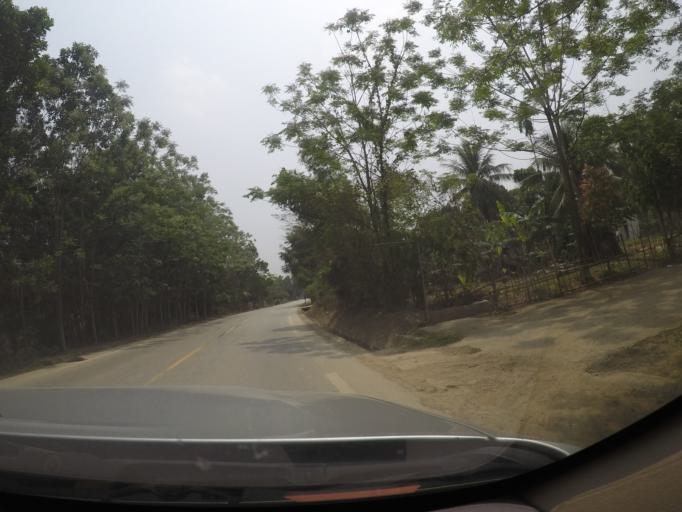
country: VN
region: Thanh Hoa
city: Thi Tran Yen Cat
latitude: 19.7378
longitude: 105.4266
